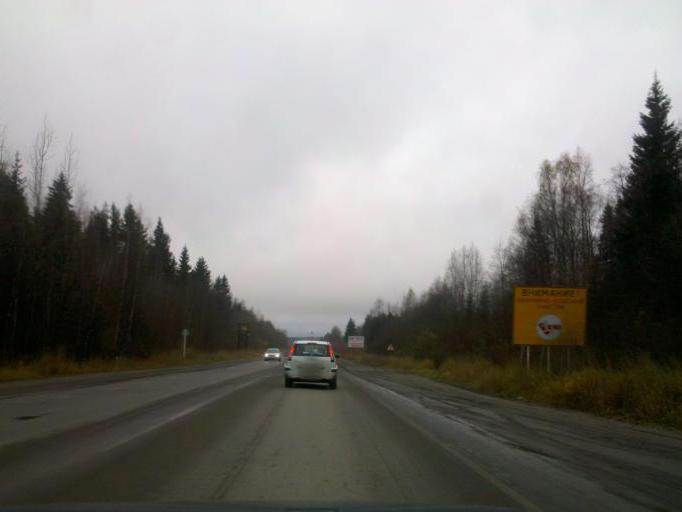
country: RU
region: Republic of Karelia
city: Shuya
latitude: 61.8252
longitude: 34.2149
